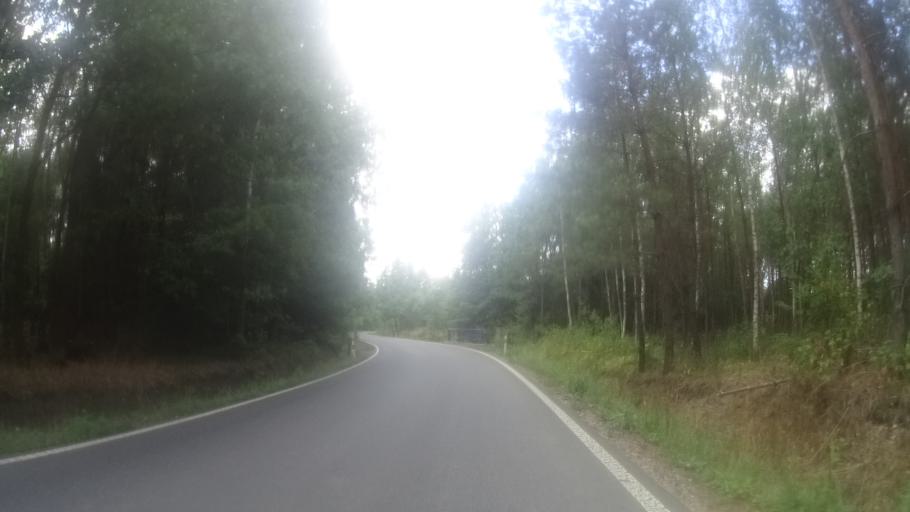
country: CZ
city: Borohradek
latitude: 50.0806
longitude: 16.1209
